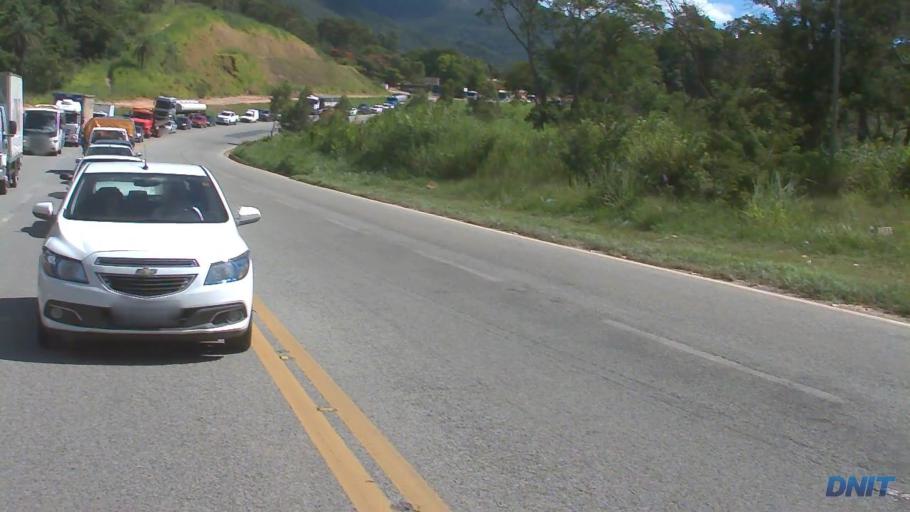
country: BR
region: Minas Gerais
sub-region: Caete
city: Caete
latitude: -19.7811
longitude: -43.6597
